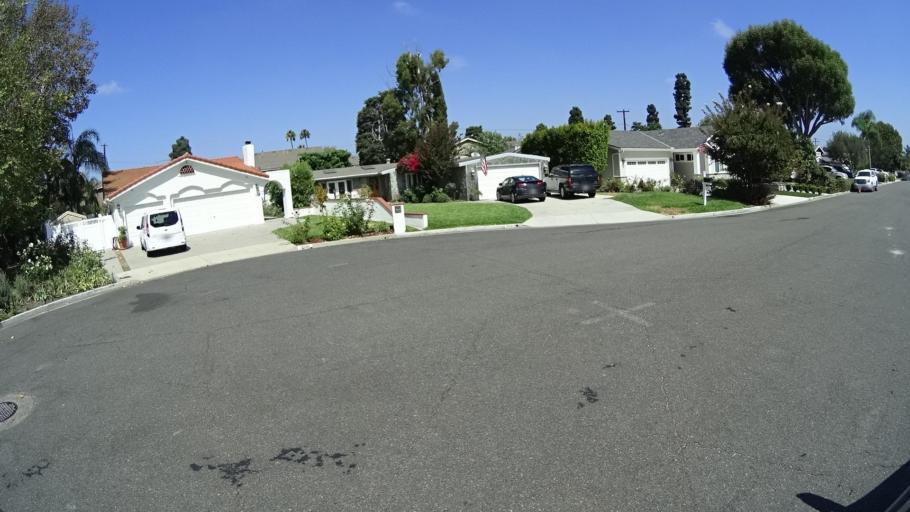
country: US
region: California
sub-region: Orange County
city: Costa Mesa
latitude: 33.6555
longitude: -117.8892
